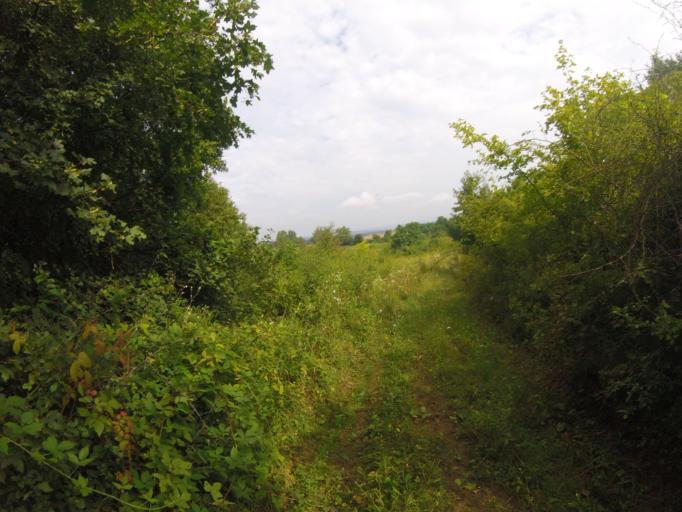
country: SK
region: Nitriansky
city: Sahy
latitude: 48.0473
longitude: 18.9243
